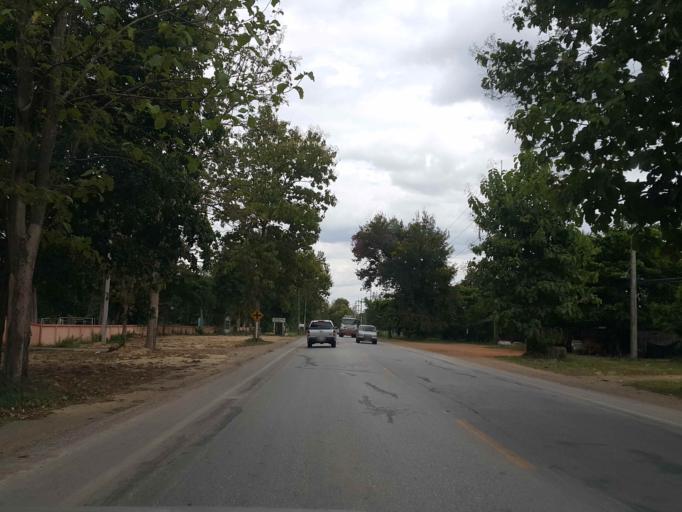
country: TH
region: Chiang Mai
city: Doi Lo
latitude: 18.4341
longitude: 98.8708
